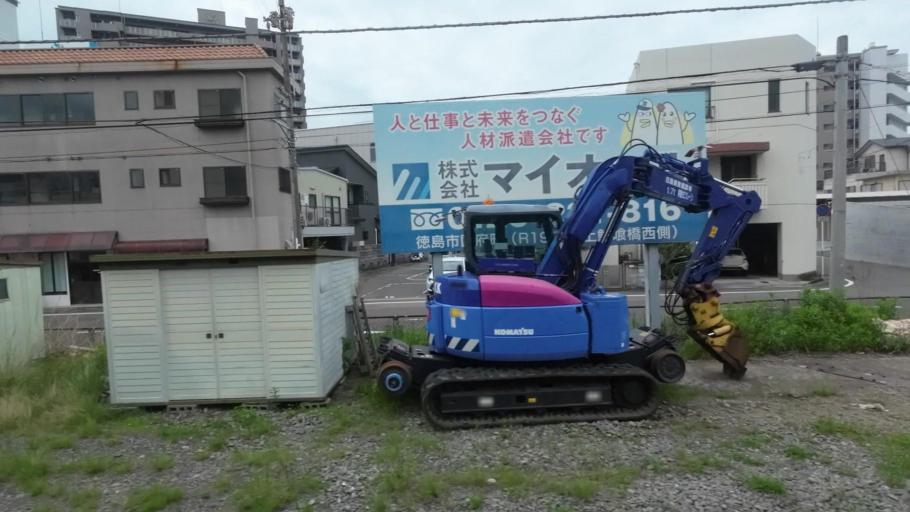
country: JP
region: Tokushima
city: Tokushima-shi
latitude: 34.0766
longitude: 134.5472
